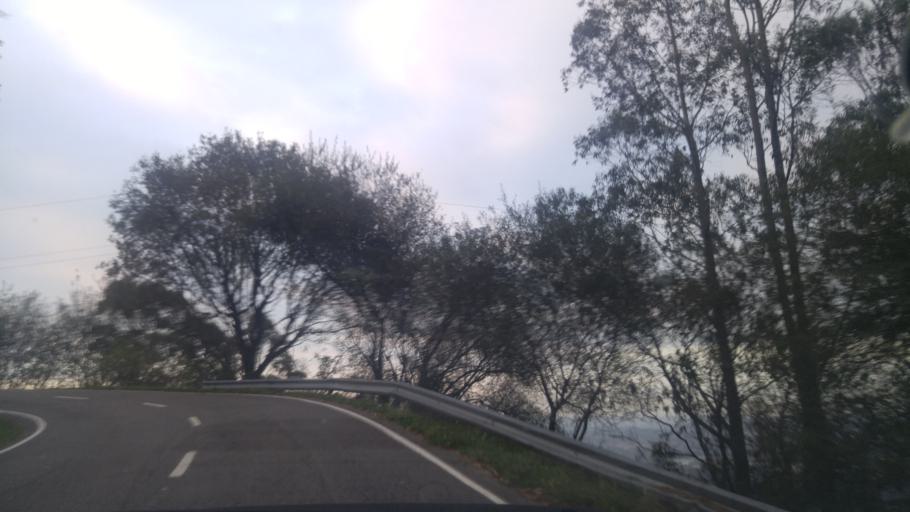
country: ES
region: Asturias
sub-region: Province of Asturias
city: Oviedo
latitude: 43.3876
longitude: -5.8516
